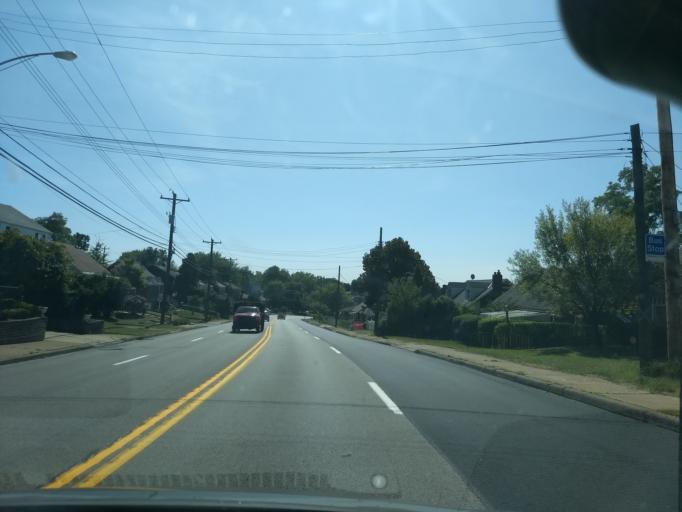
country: US
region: Pennsylvania
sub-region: Allegheny County
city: North Versailles
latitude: 40.3773
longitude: -79.8279
